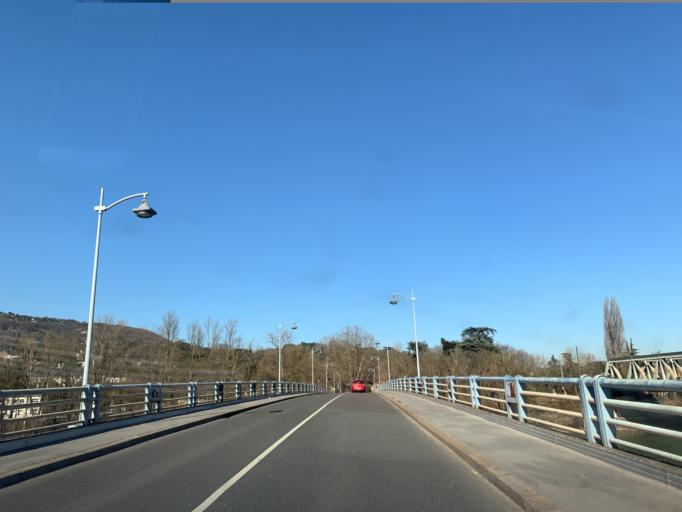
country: FR
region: Rhone-Alpes
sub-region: Departement du Rhone
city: Fontaines-sur-Saone
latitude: 45.8134
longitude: 4.8471
